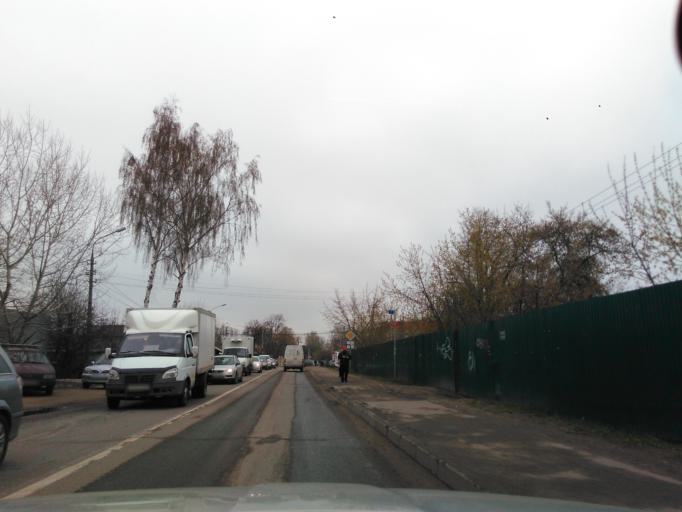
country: RU
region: Moskovskaya
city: Nakhabino
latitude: 55.8427
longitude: 37.1839
